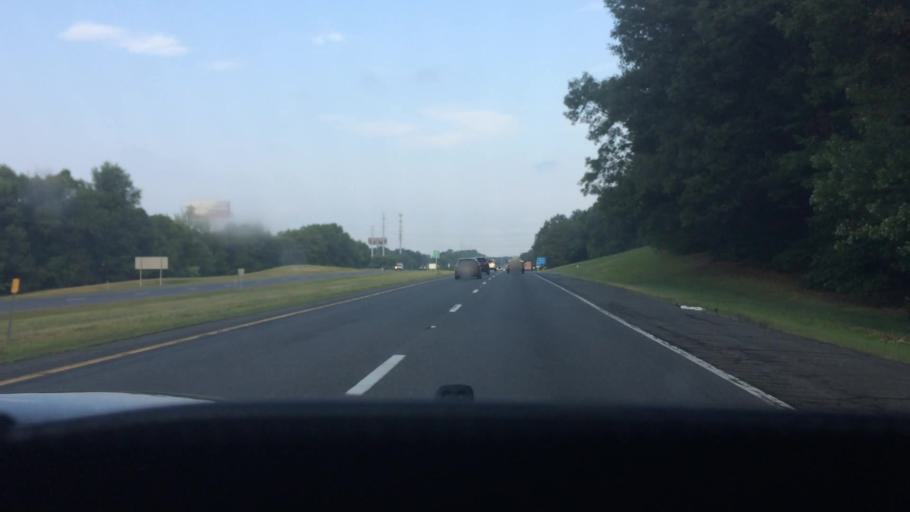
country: US
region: Massachusetts
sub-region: Hampden County
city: Ludlow
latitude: 42.1632
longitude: -72.5209
